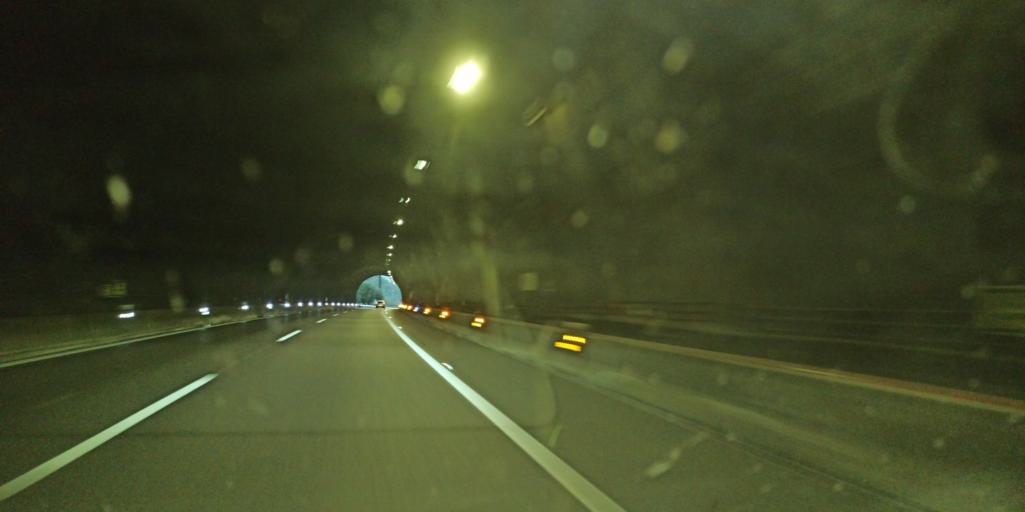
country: ES
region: Catalonia
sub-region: Provincia de Barcelona
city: Sitges
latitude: 41.2453
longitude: 1.8323
